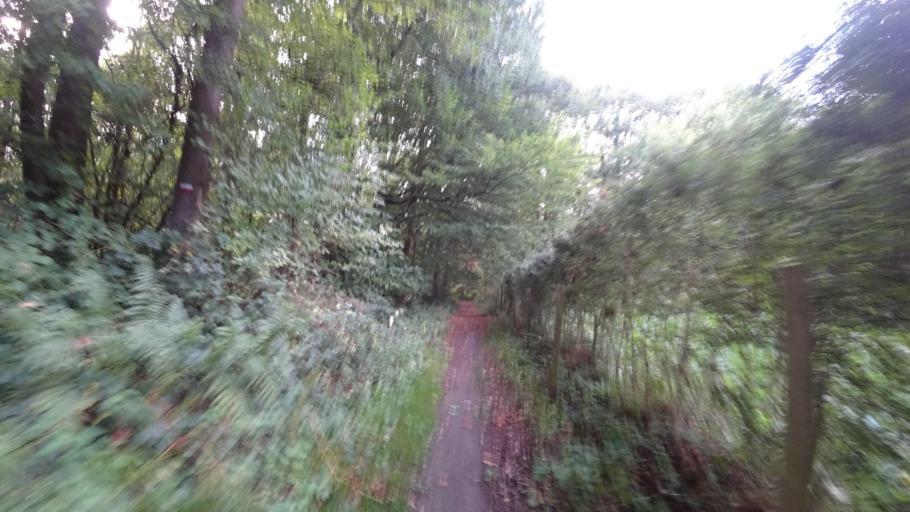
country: BE
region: Wallonia
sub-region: Province du Brabant Wallon
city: Villers-la-Ville
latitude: 50.6093
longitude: 4.5055
